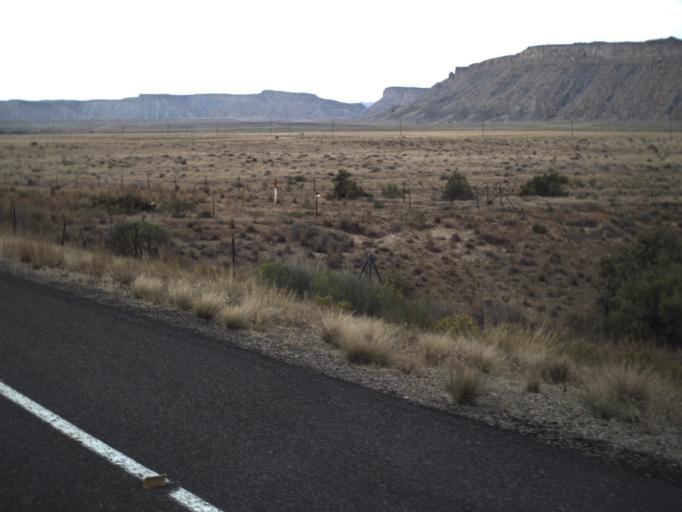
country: US
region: Utah
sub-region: Grand County
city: Moab
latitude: 38.9566
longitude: -109.7491
